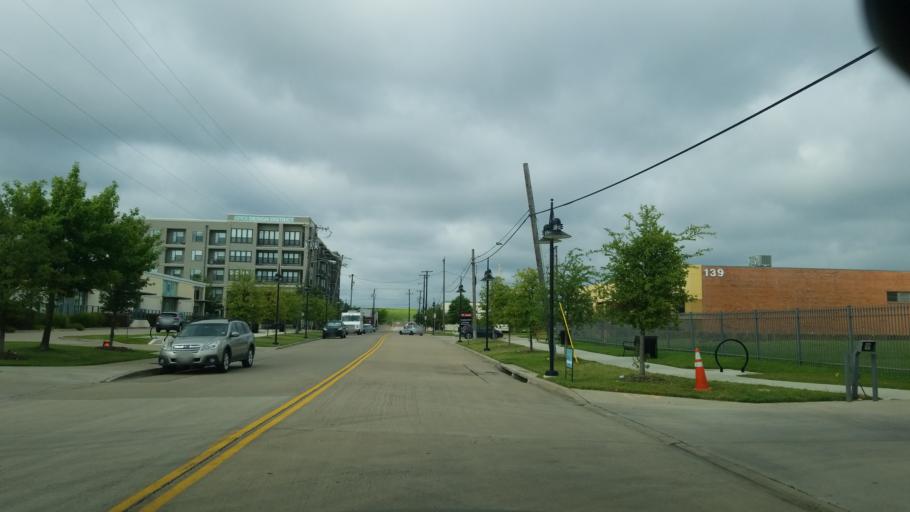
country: US
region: Texas
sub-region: Dallas County
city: Dallas
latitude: 32.7932
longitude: -96.8272
